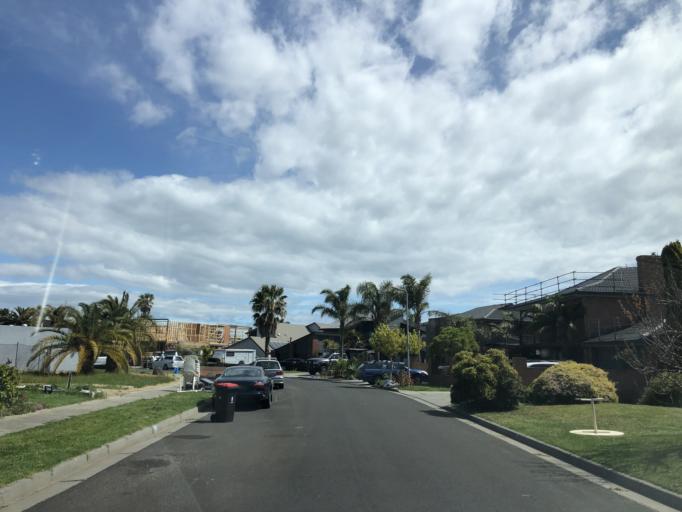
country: AU
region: Victoria
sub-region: Kingston
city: Patterson Lakes
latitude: -38.0751
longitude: 145.1431
